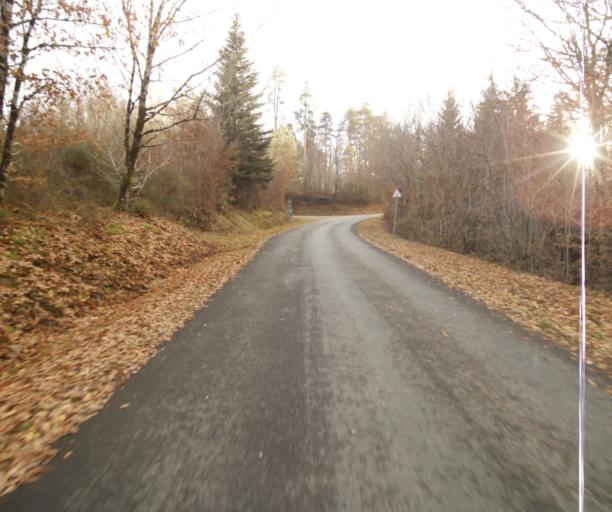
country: FR
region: Limousin
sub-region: Departement de la Correze
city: Laguenne
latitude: 45.2408
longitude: 1.7783
